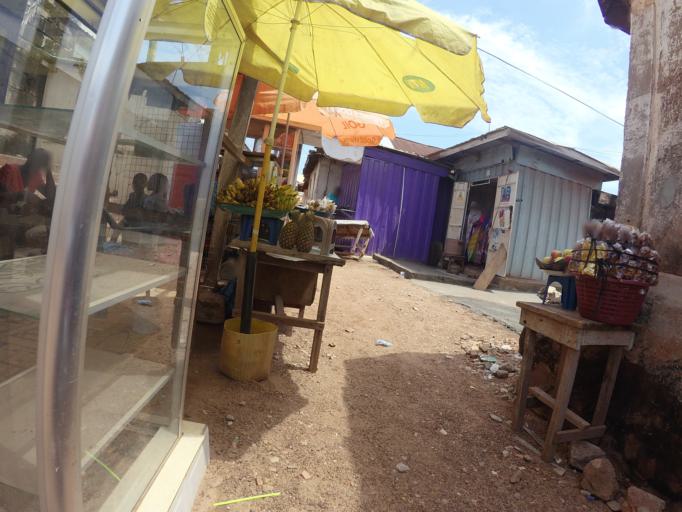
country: GH
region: Greater Accra
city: Accra
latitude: 5.5902
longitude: -0.2060
